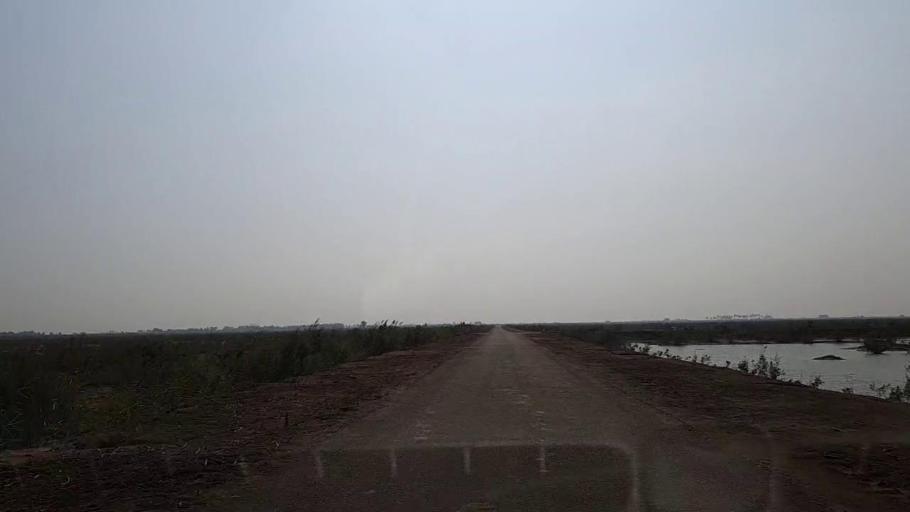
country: PK
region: Sindh
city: Gharo
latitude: 24.6686
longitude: 67.6954
